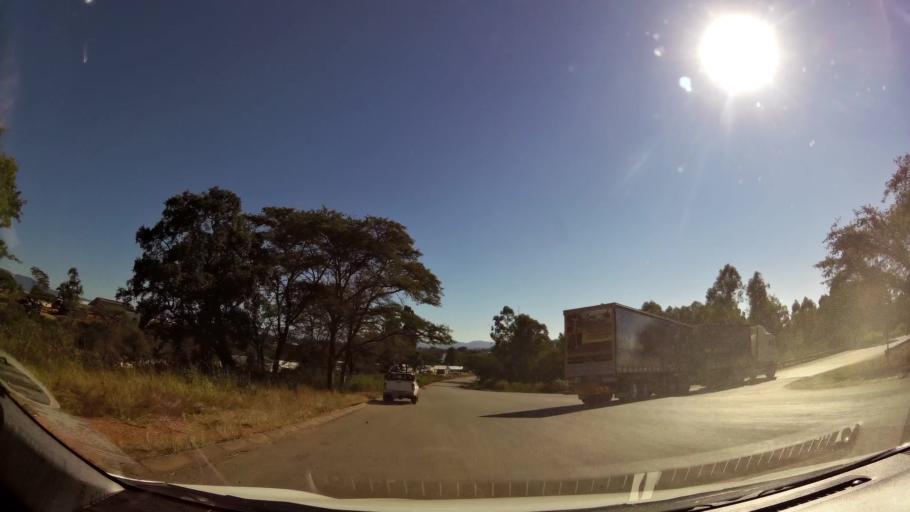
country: ZA
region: Limpopo
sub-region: Mopani District Municipality
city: Tzaneen
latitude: -23.8558
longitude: 30.1689
